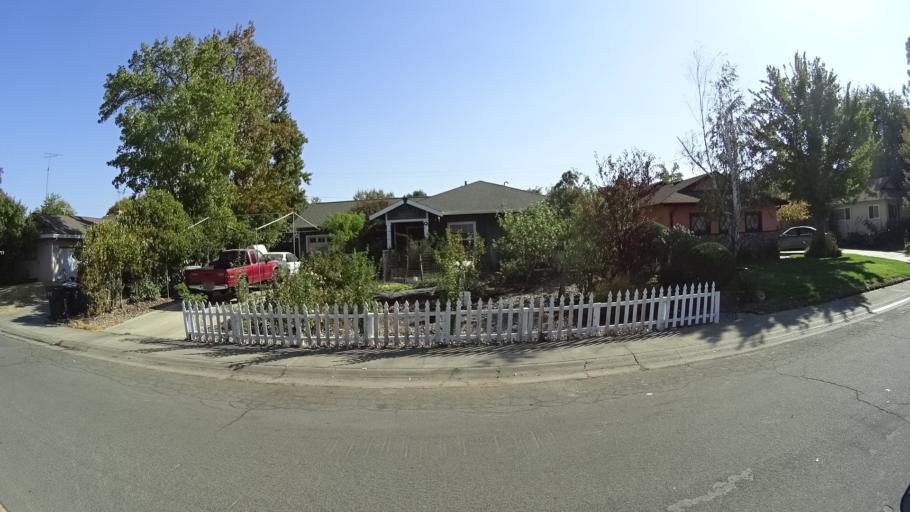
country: US
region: California
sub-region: Sacramento County
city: Parkway
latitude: 38.4868
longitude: -121.4999
